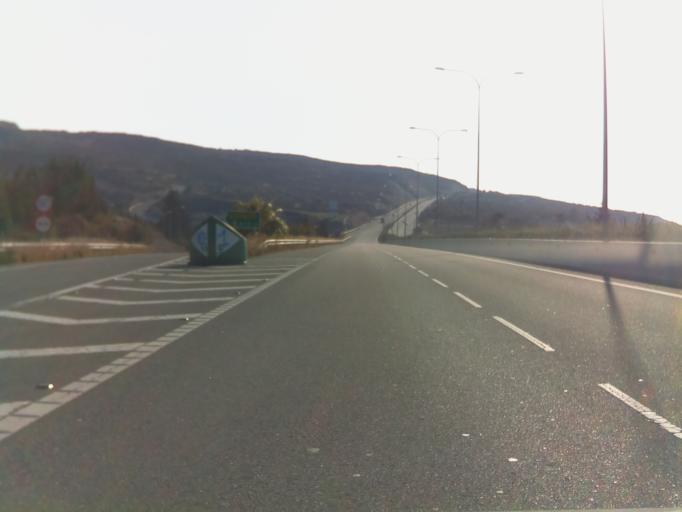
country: CY
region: Limassol
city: Pissouri
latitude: 34.6870
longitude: 32.5858
